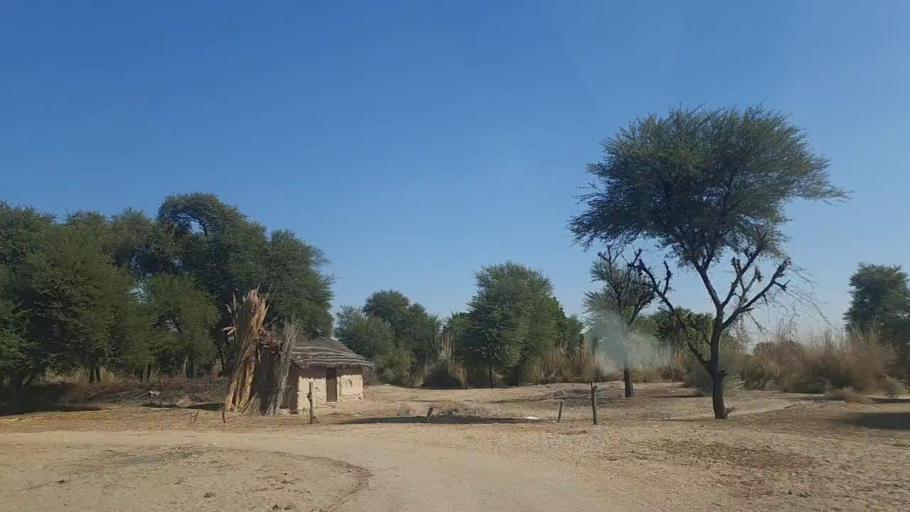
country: PK
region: Sindh
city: Khadro
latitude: 26.1482
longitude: 68.8387
